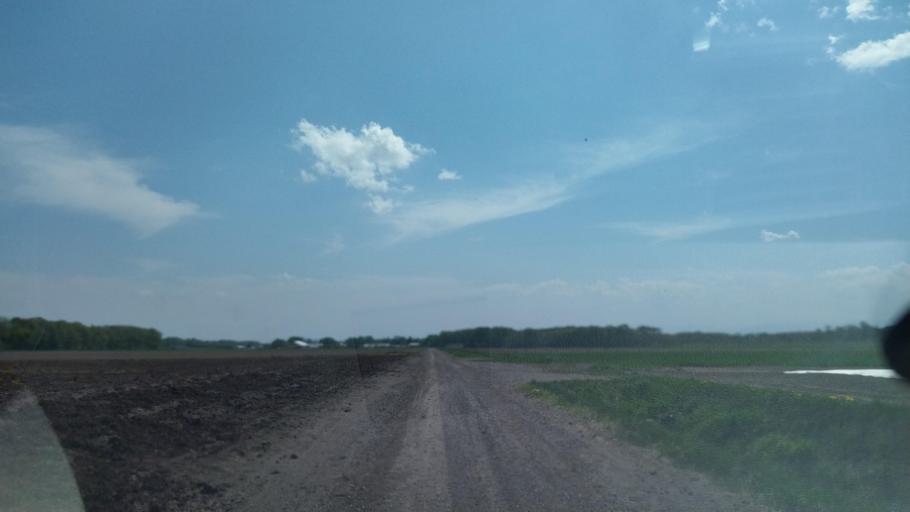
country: JP
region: Hokkaido
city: Otofuke
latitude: 43.1413
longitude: 143.2209
